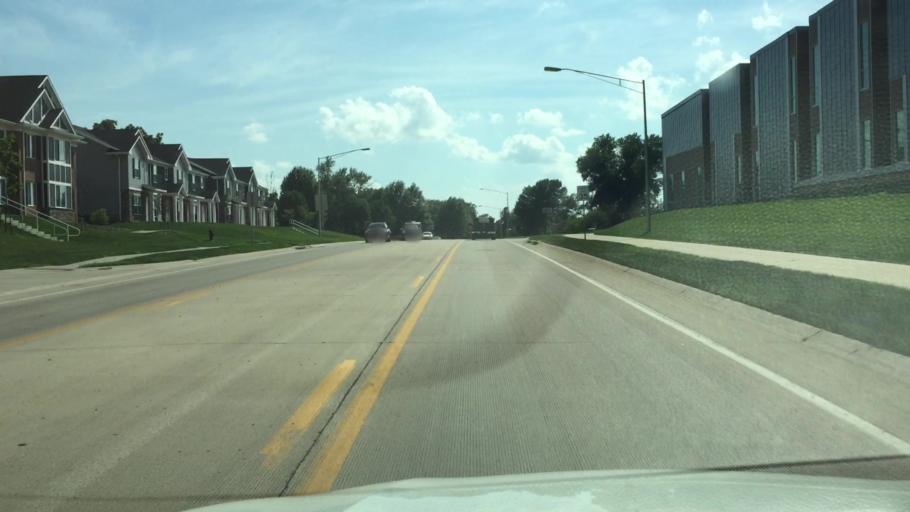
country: US
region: Iowa
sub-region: Johnson County
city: Iowa City
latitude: 41.6777
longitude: -91.5152
